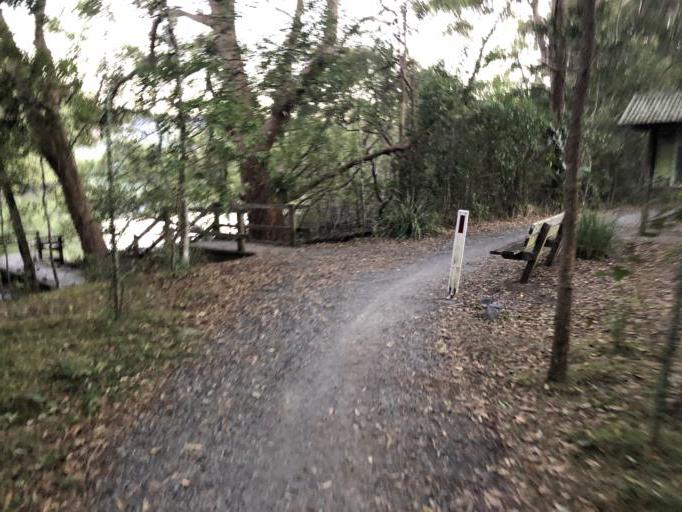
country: AU
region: New South Wales
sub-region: Coffs Harbour
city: Coffs Harbour
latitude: -30.2951
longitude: 153.1277
